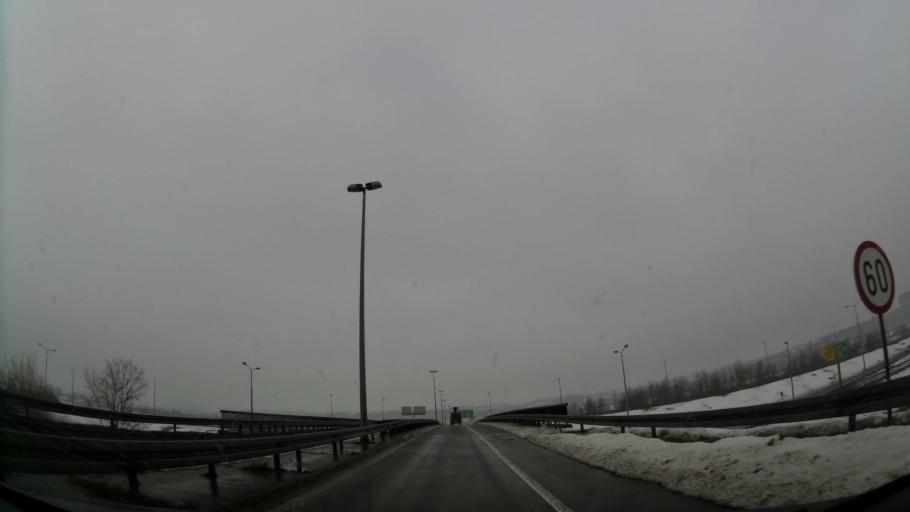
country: RS
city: Ostruznica
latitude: 44.7379
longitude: 20.3363
